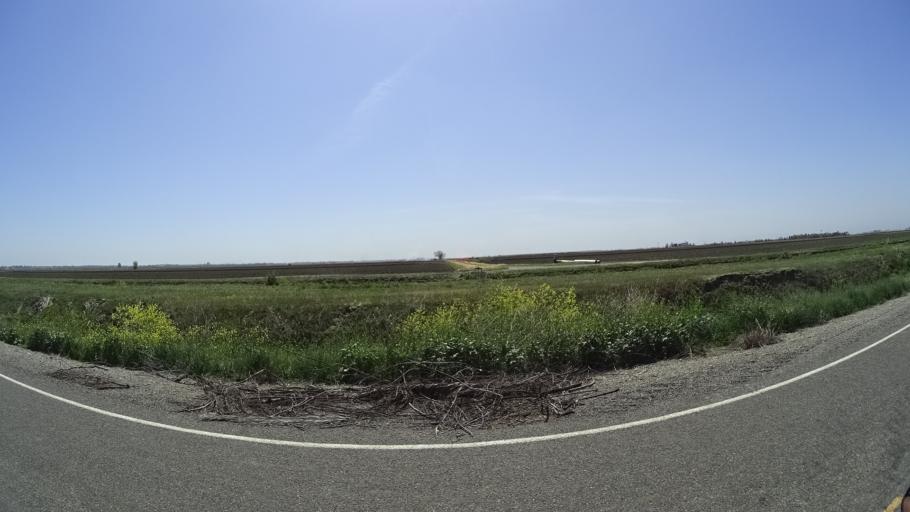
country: US
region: California
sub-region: Glenn County
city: Willows
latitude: 39.5581
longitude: -122.0415
